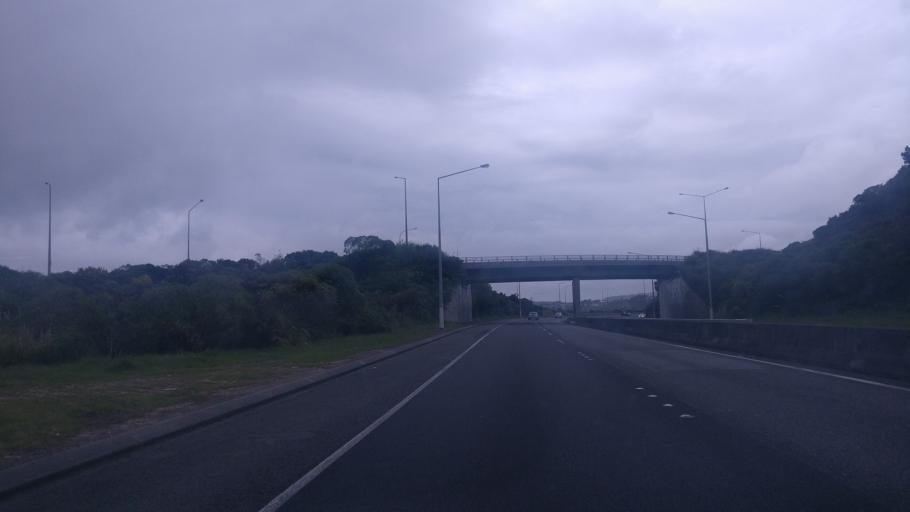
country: NZ
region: Wellington
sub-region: Porirua City
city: Porirua
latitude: -41.1326
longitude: 174.8443
